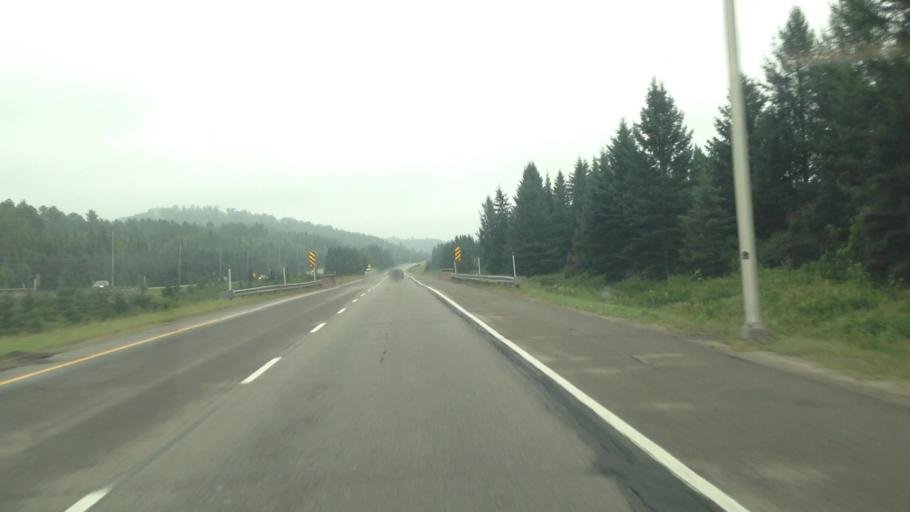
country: CA
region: Quebec
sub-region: Laurentides
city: Sainte-Agathe-des-Monts
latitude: 46.0968
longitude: -74.3541
